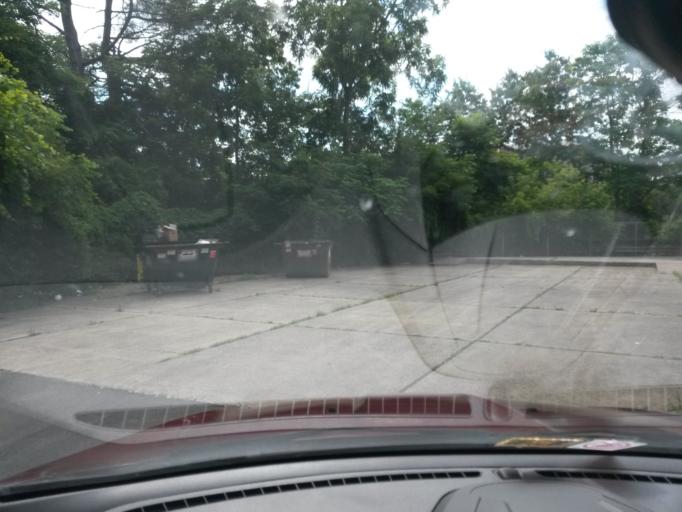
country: US
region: West Virginia
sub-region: Raleigh County
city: Beckley
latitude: 37.7780
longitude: -81.1932
